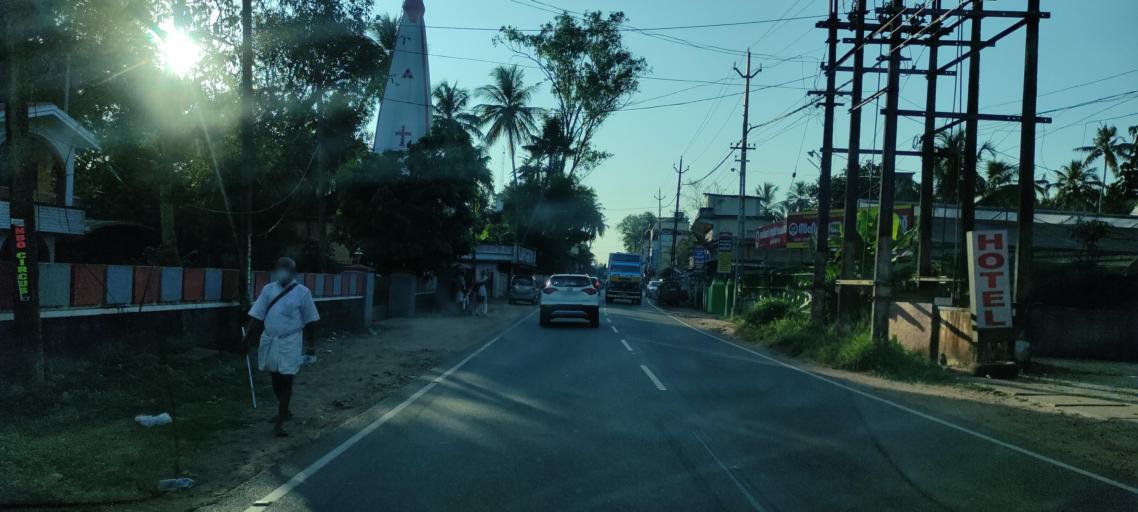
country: IN
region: Kerala
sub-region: Alappuzha
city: Kattanam
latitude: 9.1772
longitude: 76.5557
